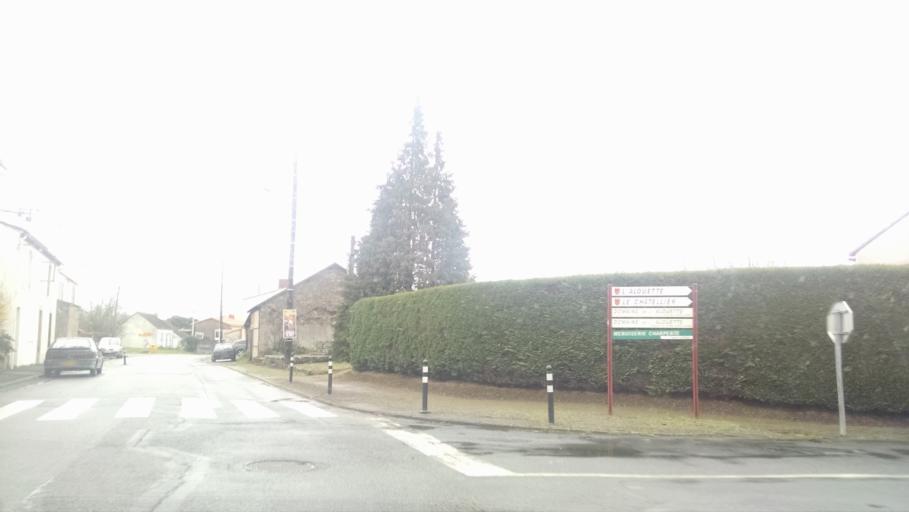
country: FR
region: Pays de la Loire
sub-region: Departement de la Loire-Atlantique
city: Maisdon-sur-Sevre
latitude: 47.0986
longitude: -1.3828
